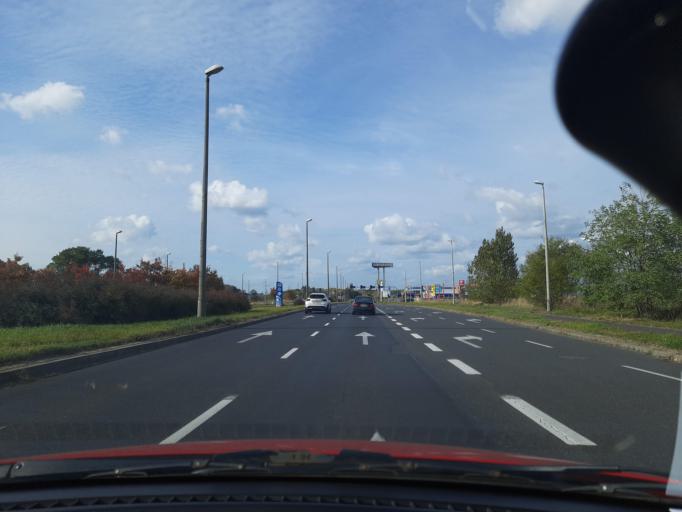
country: PL
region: Kujawsko-Pomorskie
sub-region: Powiat torunski
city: Wielka Nieszawka
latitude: 53.0164
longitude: 18.5387
